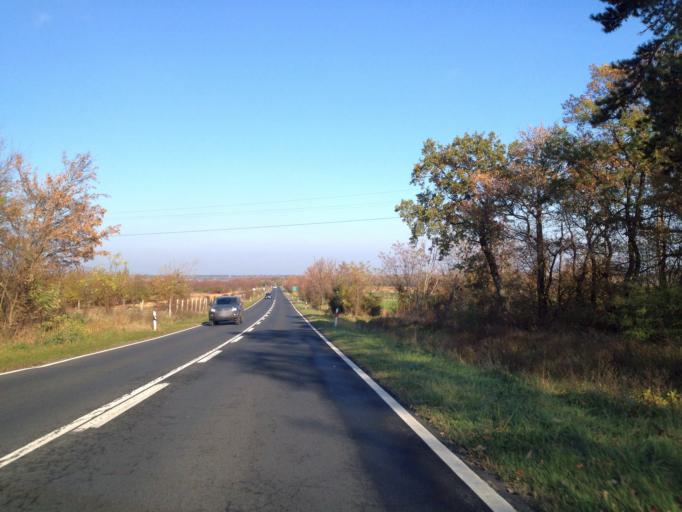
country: HU
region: Veszprem
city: Veszprem
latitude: 47.0510
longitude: 17.9203
